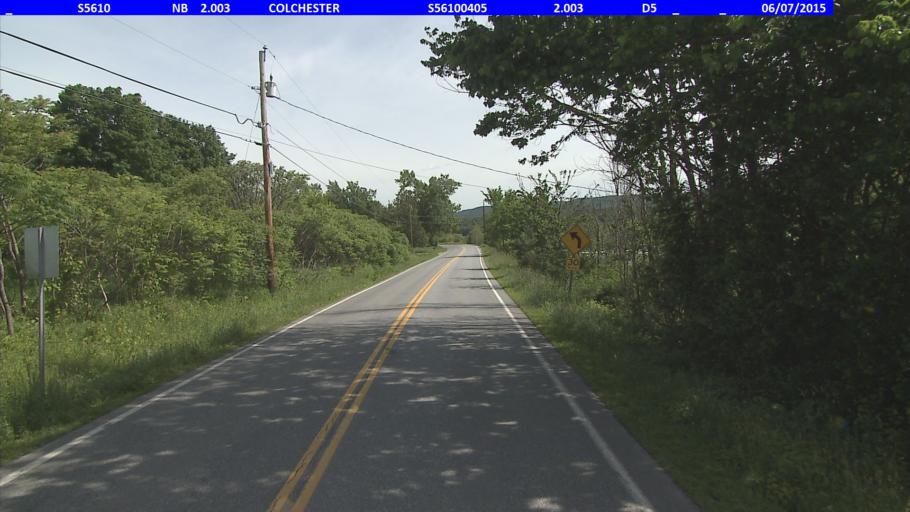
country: US
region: Vermont
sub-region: Chittenden County
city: Colchester
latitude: 44.5685
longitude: -73.1282
